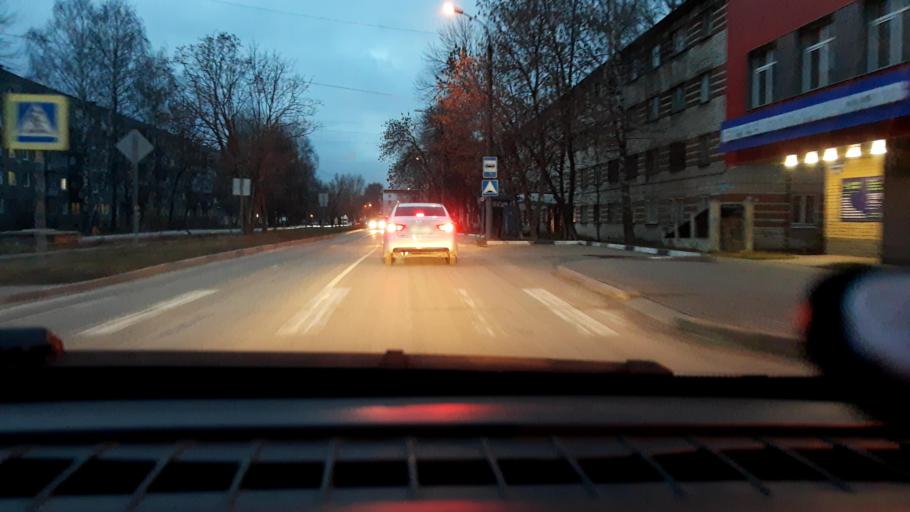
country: RU
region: Nizjnij Novgorod
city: Kstovo
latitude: 56.1404
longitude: 44.1924
